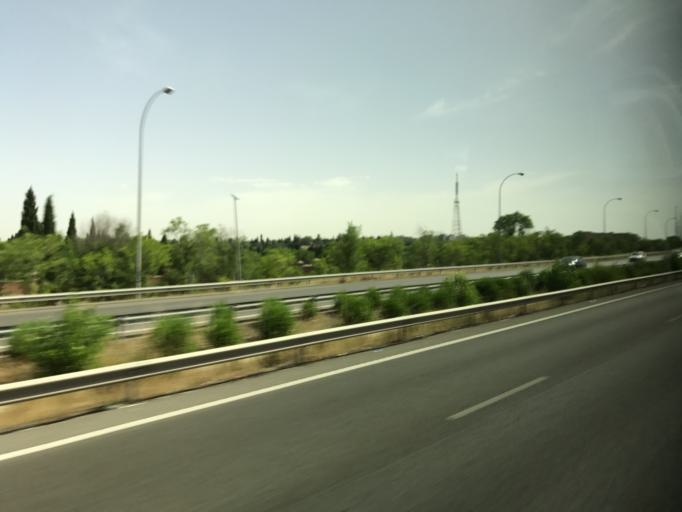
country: ES
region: Madrid
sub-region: Provincia de Madrid
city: Moratalaz
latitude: 40.4143
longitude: -3.6409
